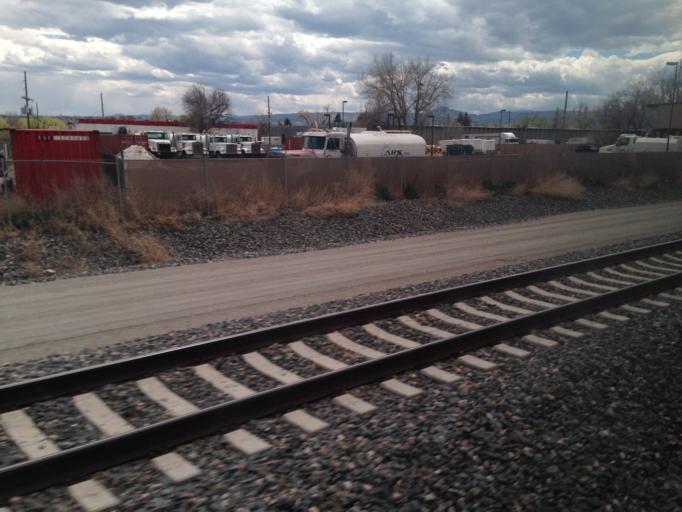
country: US
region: Colorado
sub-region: Jefferson County
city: Arvada
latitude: 39.7908
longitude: -105.1193
